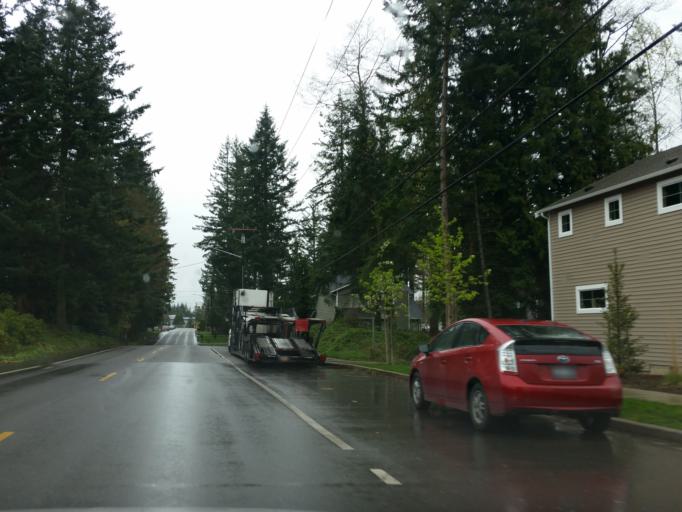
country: US
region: Washington
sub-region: Snohomish County
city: Martha Lake
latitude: 47.8730
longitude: -122.2474
